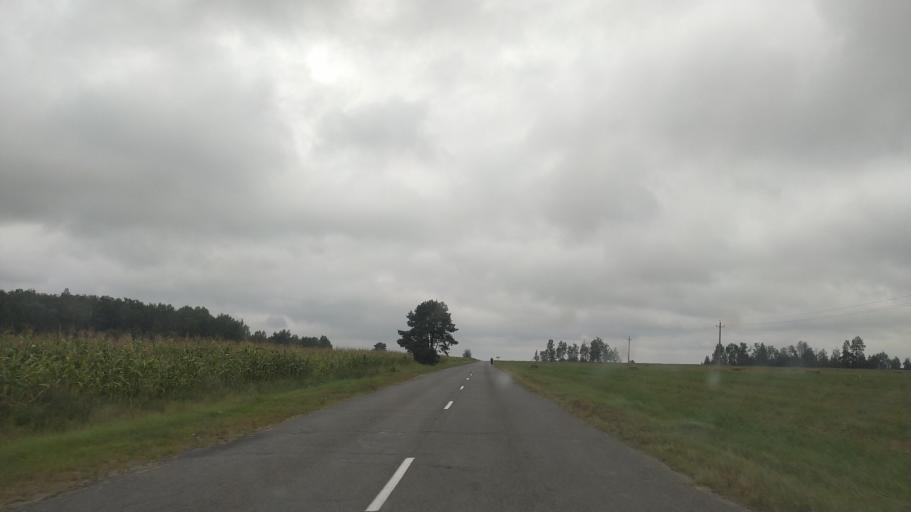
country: BY
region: Brest
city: Byaroza
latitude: 52.5628
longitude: 24.9055
